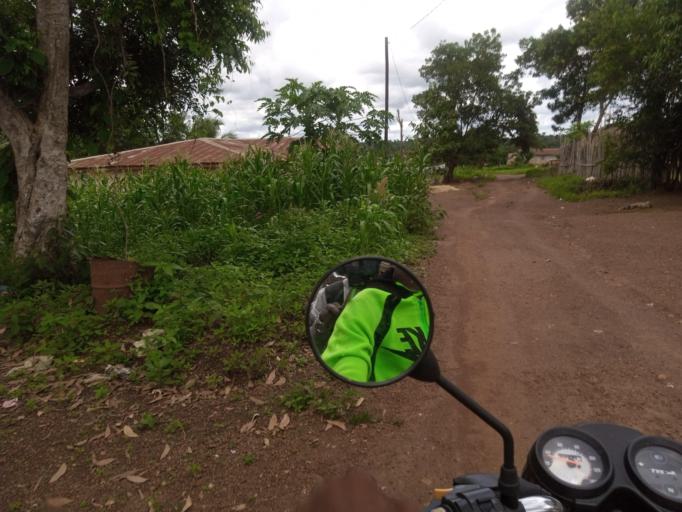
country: SL
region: Northern Province
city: Port Loko
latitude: 8.7599
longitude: -12.7781
